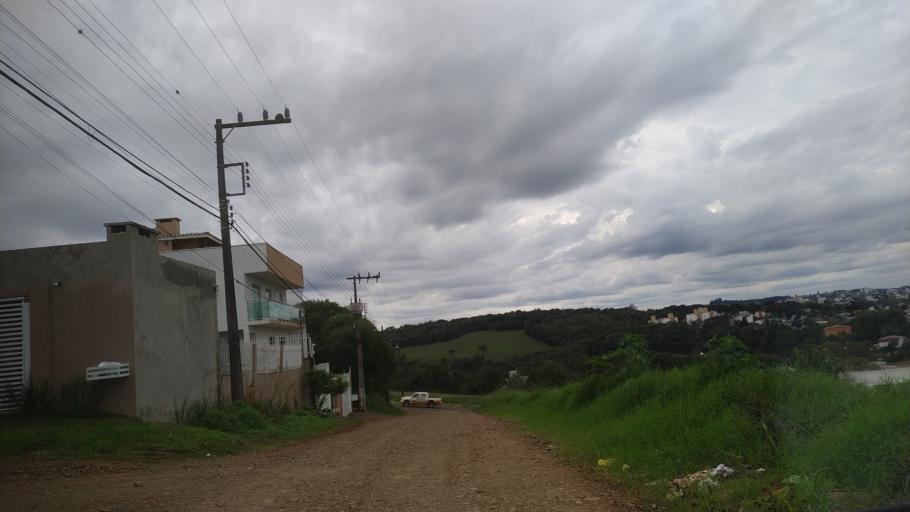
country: BR
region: Santa Catarina
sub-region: Chapeco
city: Chapeco
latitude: -27.0702
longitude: -52.6061
